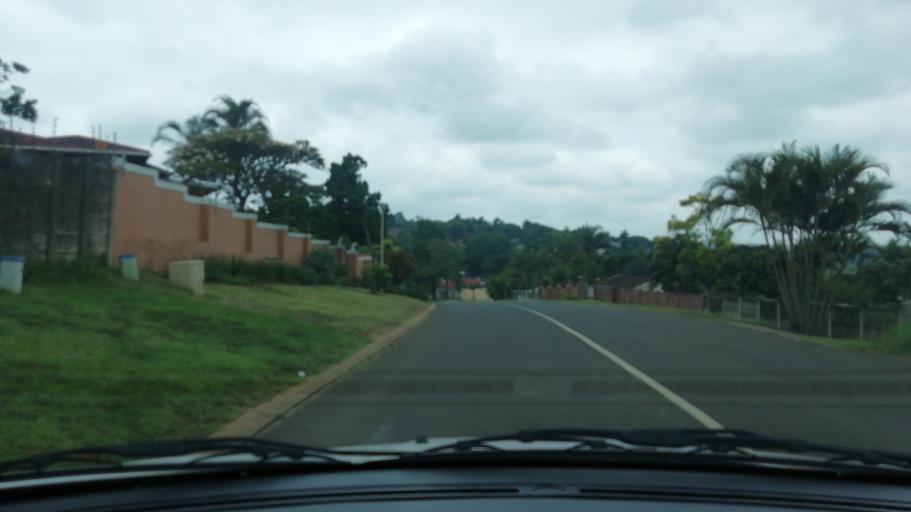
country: ZA
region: KwaZulu-Natal
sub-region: uThungulu District Municipality
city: Empangeni
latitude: -28.7624
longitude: 31.8857
